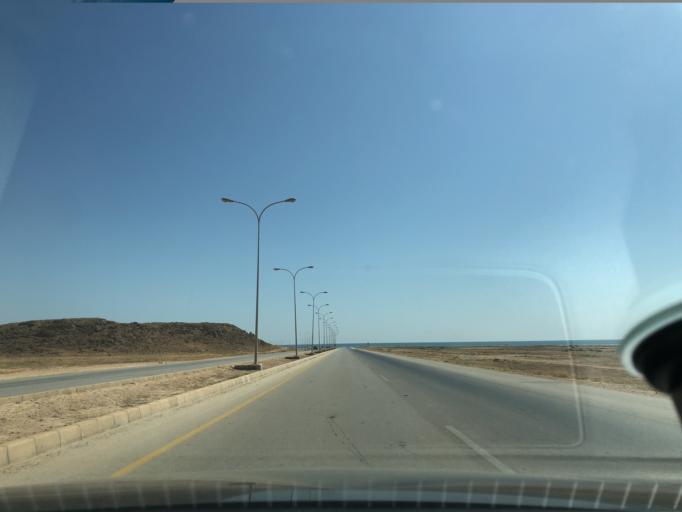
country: OM
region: Zufar
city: Salalah
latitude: 17.0415
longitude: 54.3389
